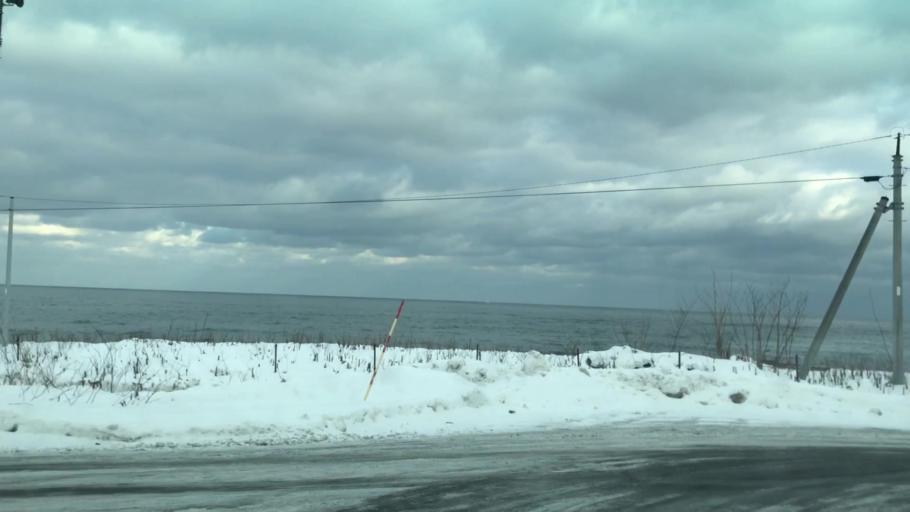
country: JP
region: Hokkaido
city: Yoichi
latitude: 43.2540
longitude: 140.6830
